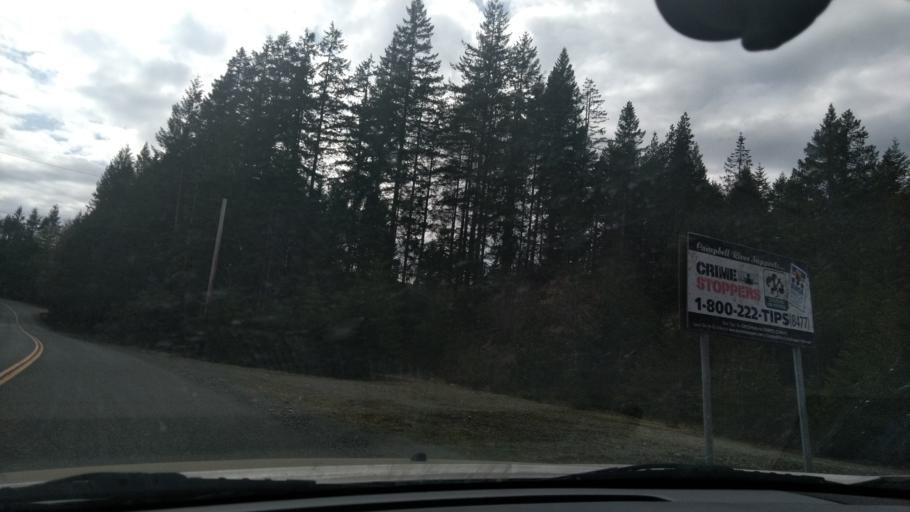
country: CA
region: British Columbia
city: Campbell River
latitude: 50.0025
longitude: -125.3708
